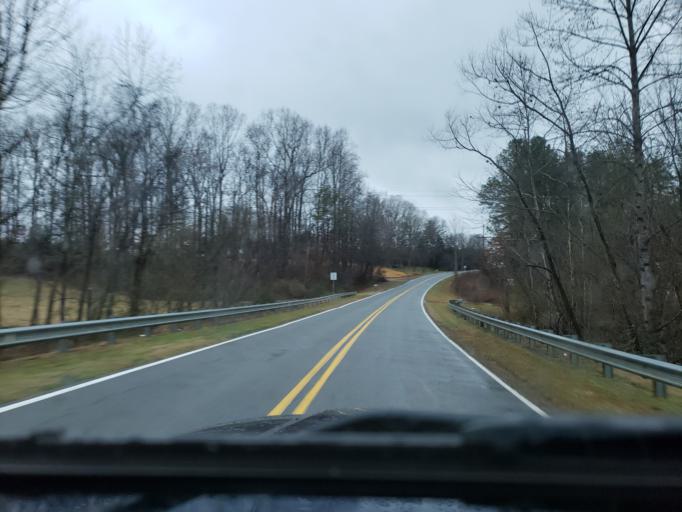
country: US
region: North Carolina
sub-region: Cleveland County
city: White Plains
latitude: 35.1821
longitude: -81.3738
